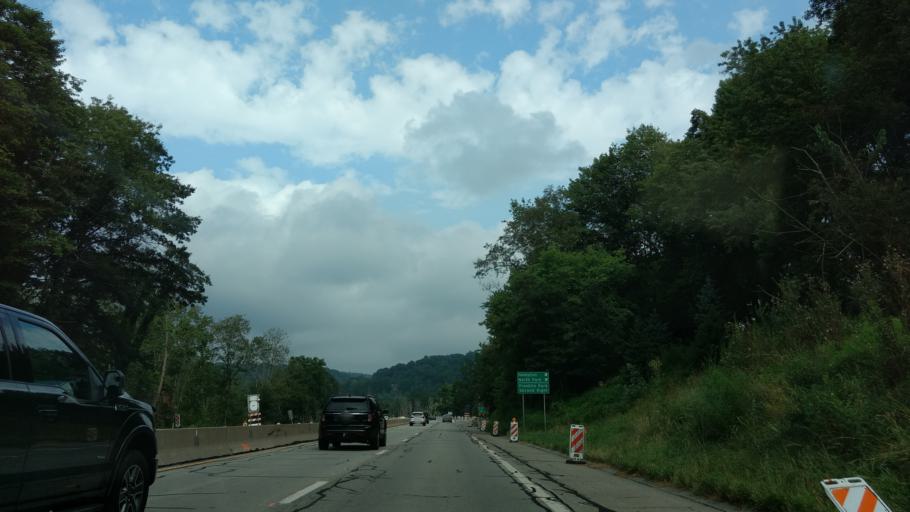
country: US
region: Pennsylvania
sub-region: Allegheny County
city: West View
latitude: 40.5810
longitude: -80.0288
